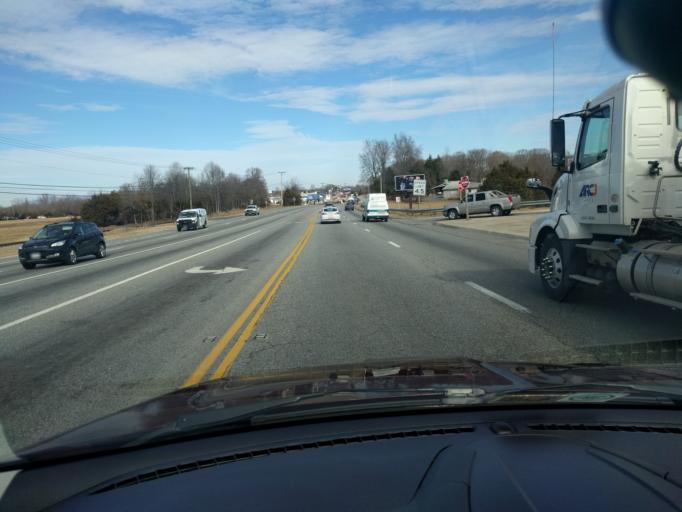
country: US
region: Virginia
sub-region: Bedford County
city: Forest
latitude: 37.3704
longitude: -79.2530
